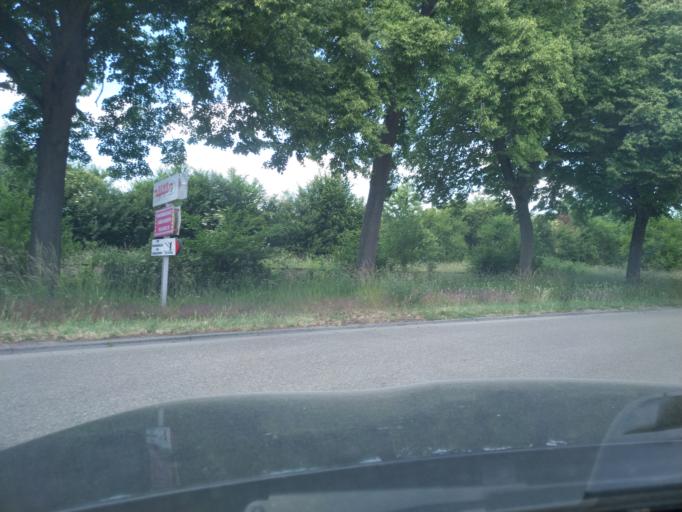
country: DE
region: Rheinland-Pfalz
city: Worth am Rhein
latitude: 49.0357
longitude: 8.2810
